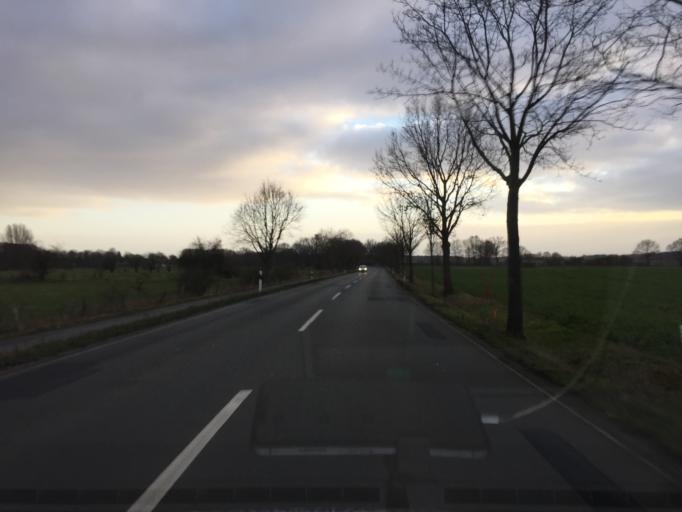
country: DE
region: Lower Saxony
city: Garbsen
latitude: 52.4511
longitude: 9.5264
